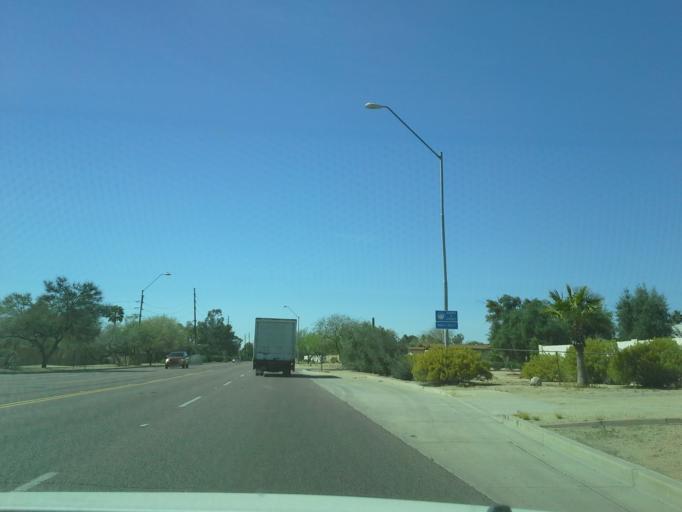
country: US
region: Arizona
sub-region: Maricopa County
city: Paradise Valley
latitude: 33.5969
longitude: -111.9438
